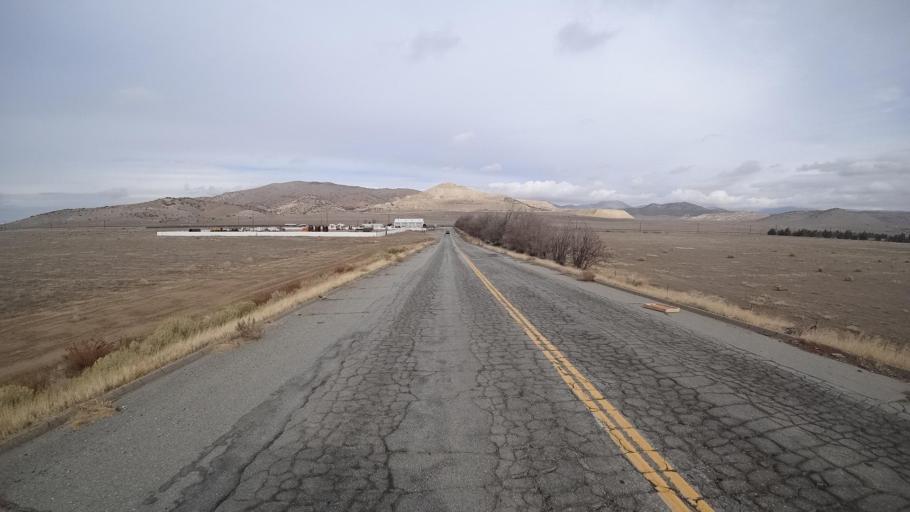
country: US
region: California
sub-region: Kern County
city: Tehachapi
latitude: 35.1219
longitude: -118.3963
